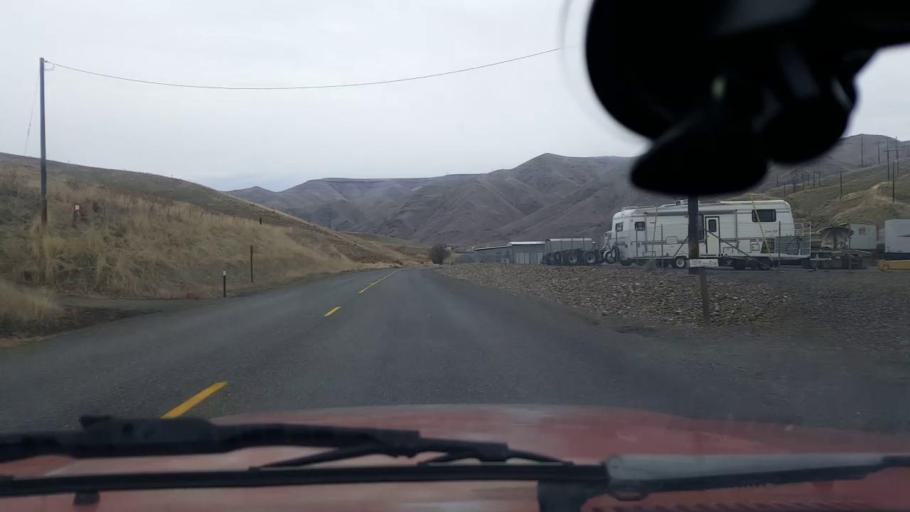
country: US
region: Washington
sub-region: Asotin County
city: Clarkston Heights-Vineland
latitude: 46.4120
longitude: -117.1120
